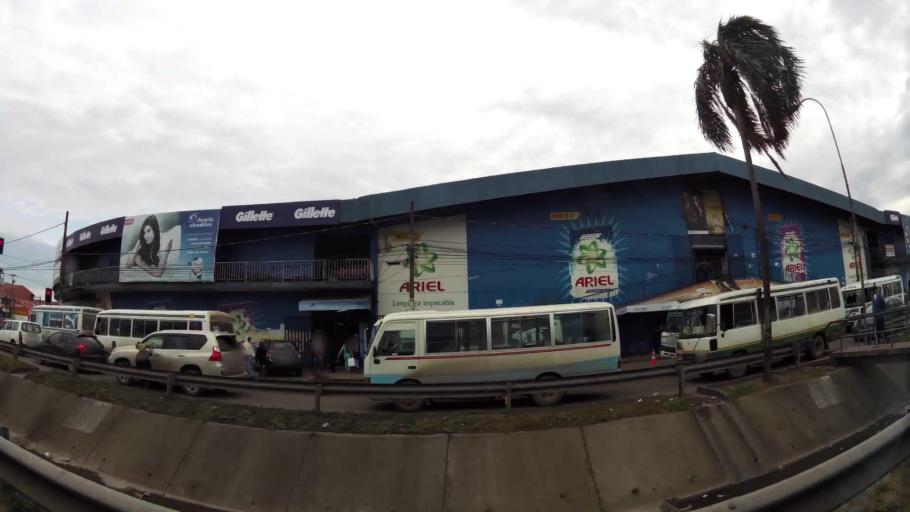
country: BO
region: Santa Cruz
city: Santa Cruz de la Sierra
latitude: -17.7642
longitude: -63.1604
